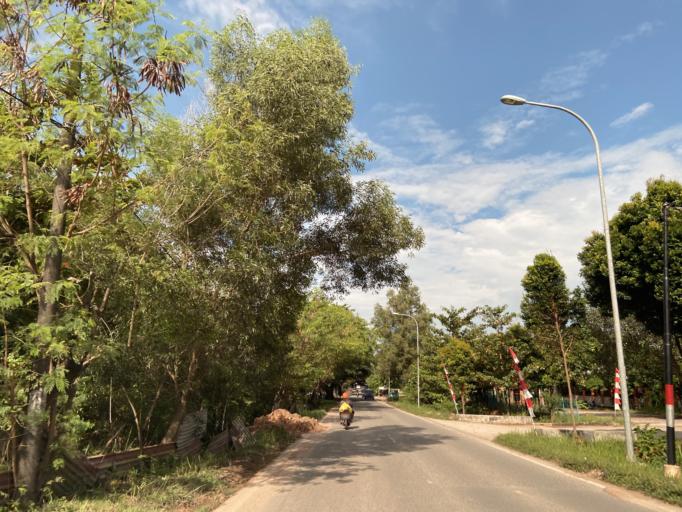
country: SG
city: Singapore
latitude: 1.1121
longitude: 104.0359
